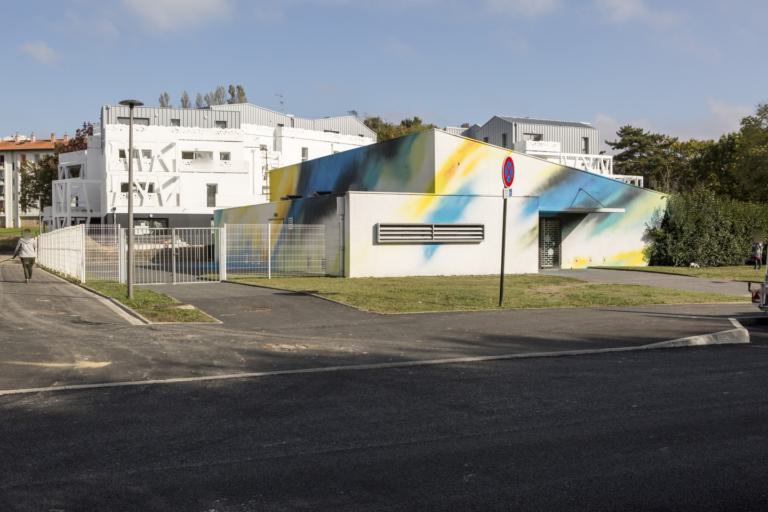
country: FR
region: Aquitaine
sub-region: Departement des Pyrenees-Atlantiques
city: Boucau
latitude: 43.5038
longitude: -1.4691
